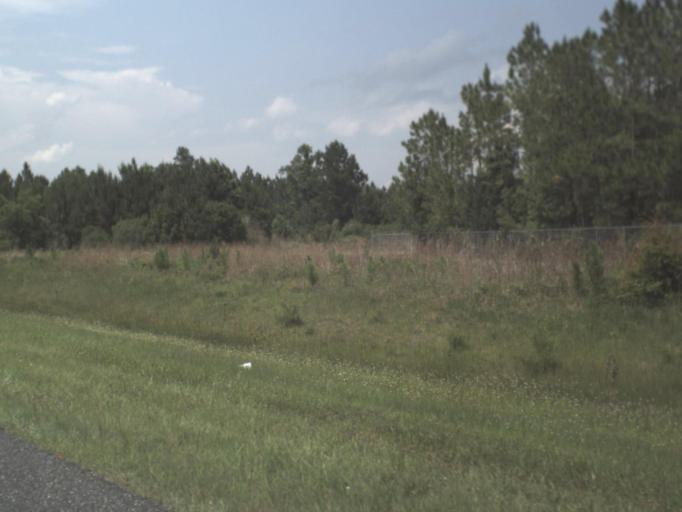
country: US
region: Florida
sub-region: Putnam County
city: Palatka
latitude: 29.8043
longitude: -81.6562
